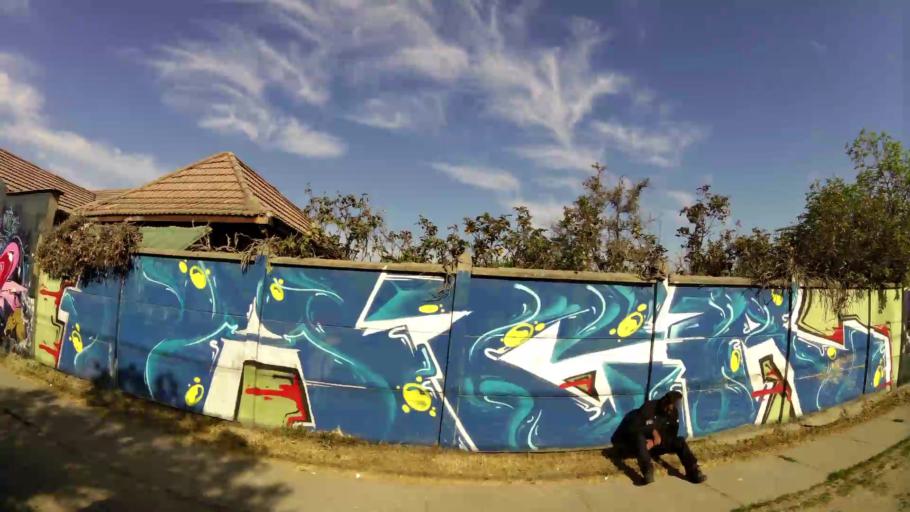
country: CL
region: Santiago Metropolitan
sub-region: Provincia de Santiago
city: La Pintana
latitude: -33.5645
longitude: -70.5908
